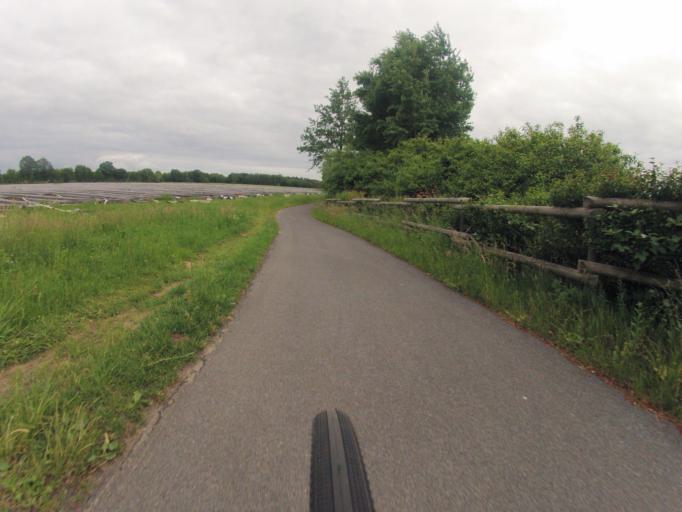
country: DE
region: North Rhine-Westphalia
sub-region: Regierungsbezirk Munster
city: Birgte
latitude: 52.2068
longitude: 7.6722
